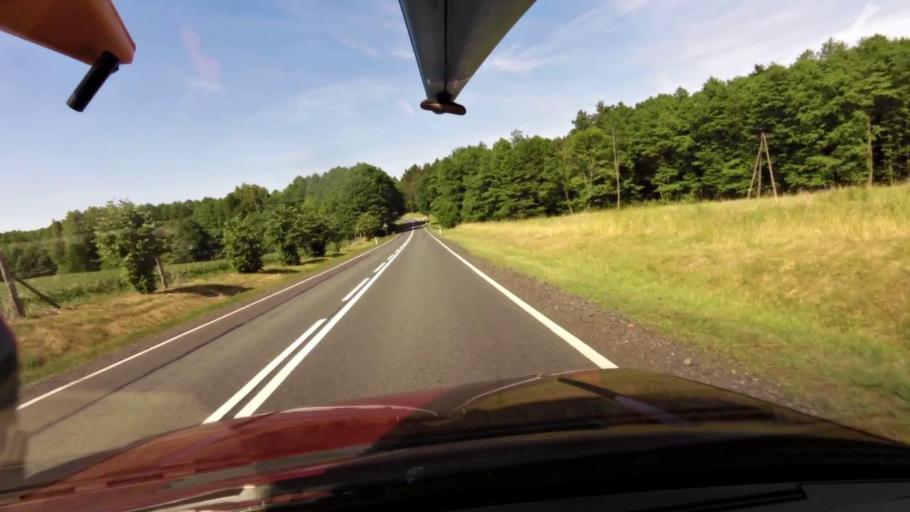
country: PL
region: Pomeranian Voivodeship
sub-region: Powiat bytowski
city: Miastko
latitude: 54.1125
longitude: 16.9969
